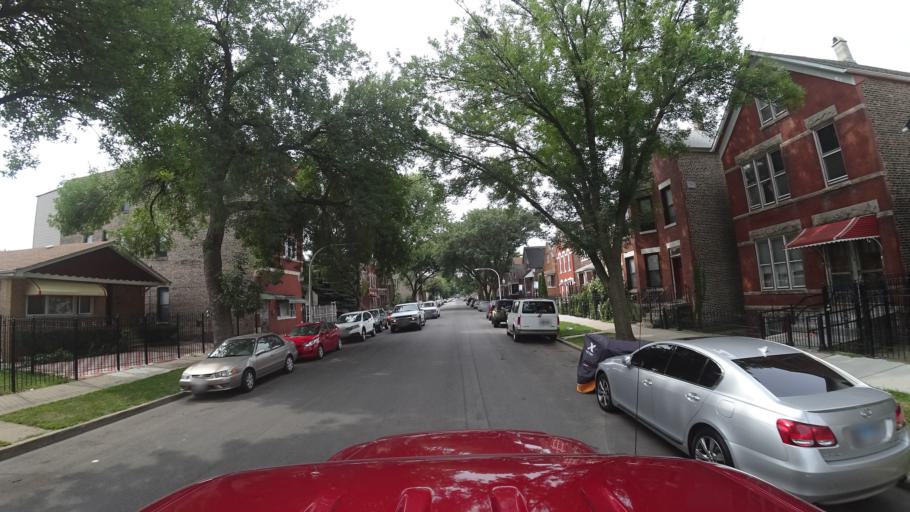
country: US
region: Illinois
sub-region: Cook County
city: Chicago
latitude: 41.8282
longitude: -87.6705
